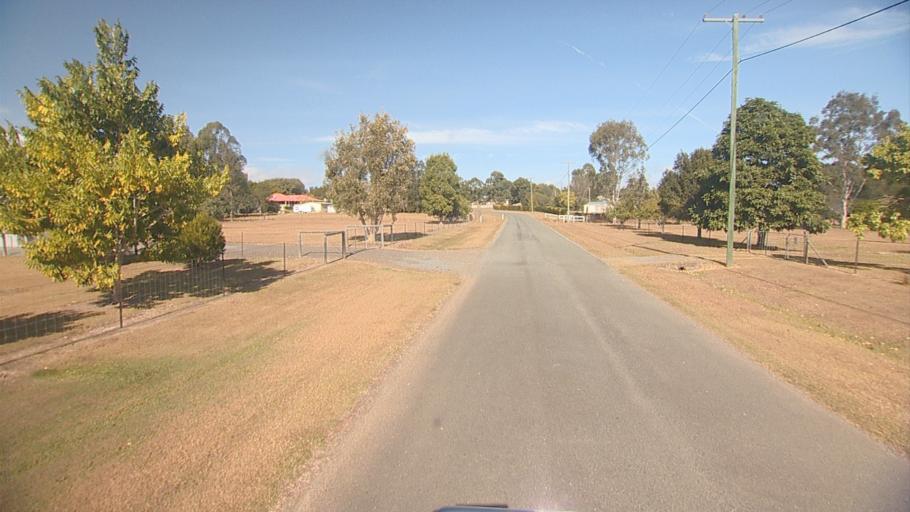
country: AU
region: Queensland
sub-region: Logan
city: Cedar Vale
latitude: -27.8685
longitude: 152.9688
